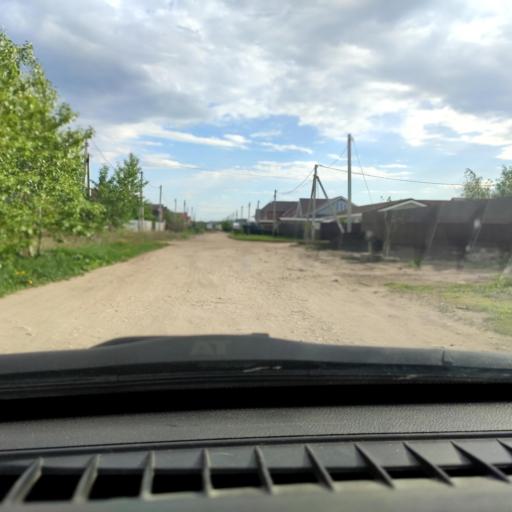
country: RU
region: Samara
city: Tol'yatti
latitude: 53.5690
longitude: 49.4105
